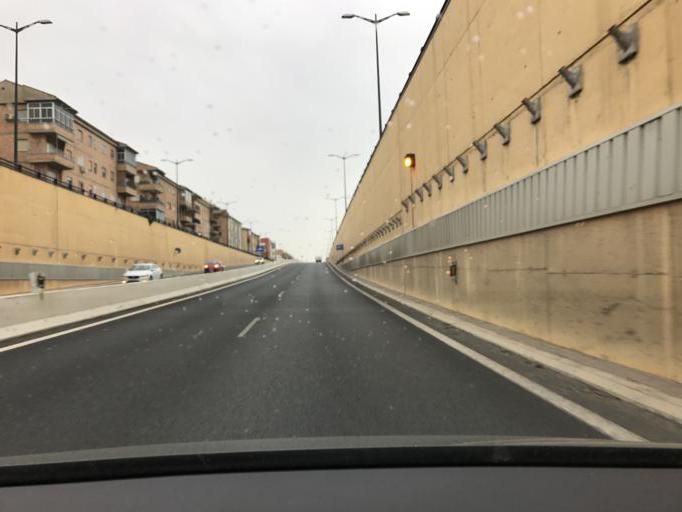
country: ES
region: Andalusia
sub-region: Provincia de Granada
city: Atarfe
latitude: 37.1925
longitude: -3.7097
